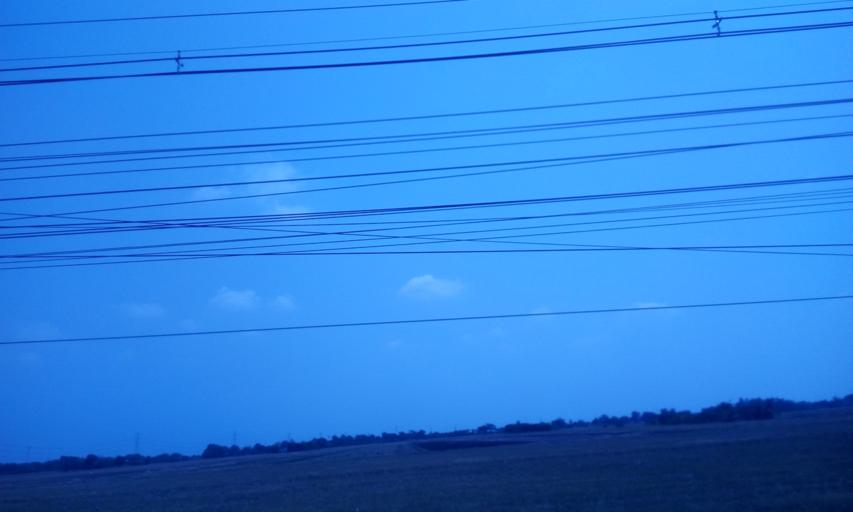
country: TH
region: Chachoengsao
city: Bang Nam Priao
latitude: 13.8158
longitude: 101.0534
